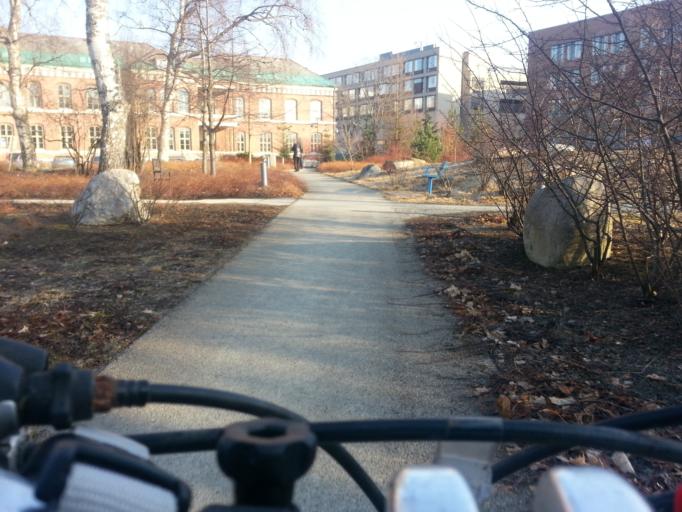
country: NO
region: Sor-Trondelag
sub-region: Trondheim
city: Trondheim
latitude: 63.4186
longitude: 10.3895
